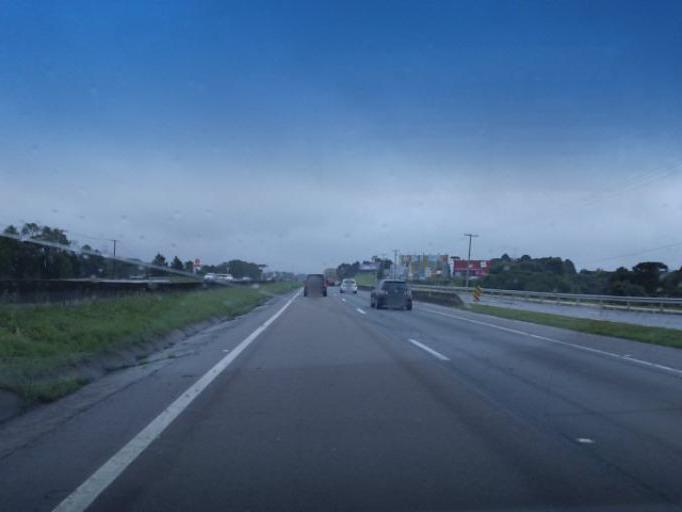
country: BR
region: Parana
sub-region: Sao Jose Dos Pinhais
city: Sao Jose dos Pinhais
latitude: -25.6793
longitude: -49.1492
